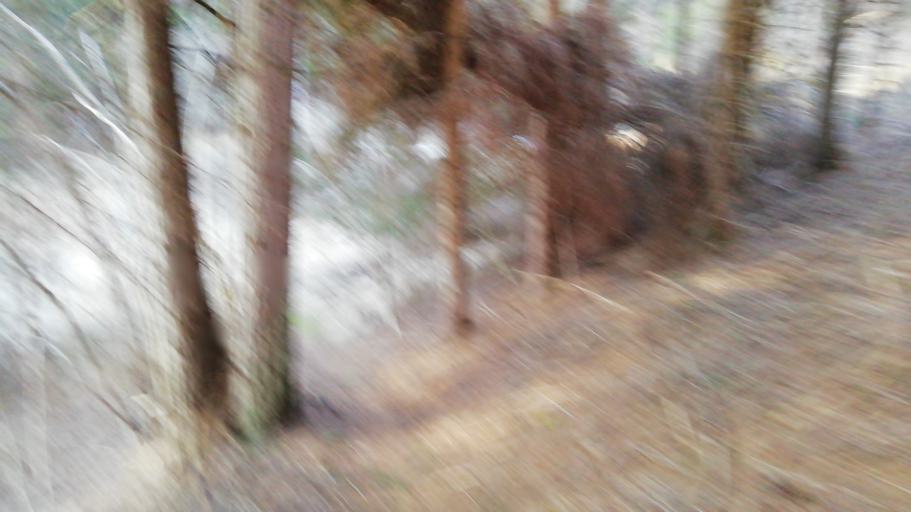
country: IT
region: Veneto
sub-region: Provincia di Belluno
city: Valle di Cadore
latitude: 46.4183
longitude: 12.3223
